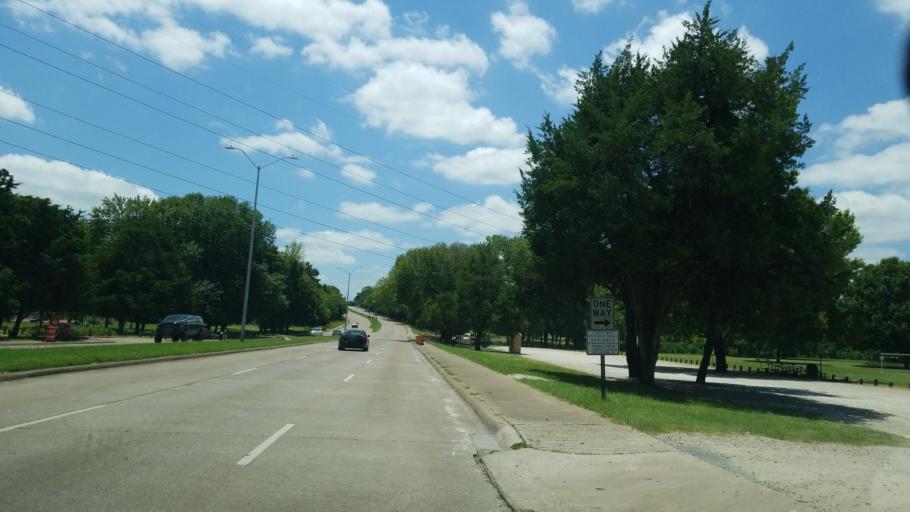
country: US
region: Texas
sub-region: Dallas County
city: Balch Springs
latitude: 32.7580
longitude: -96.7019
